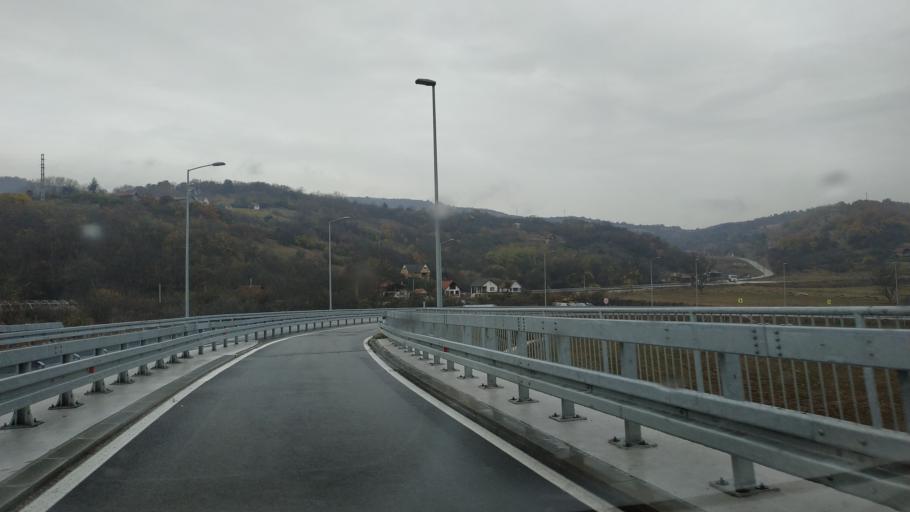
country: RS
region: Central Serbia
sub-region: Pirotski Okrug
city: Pirot
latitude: 43.1900
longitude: 22.5639
